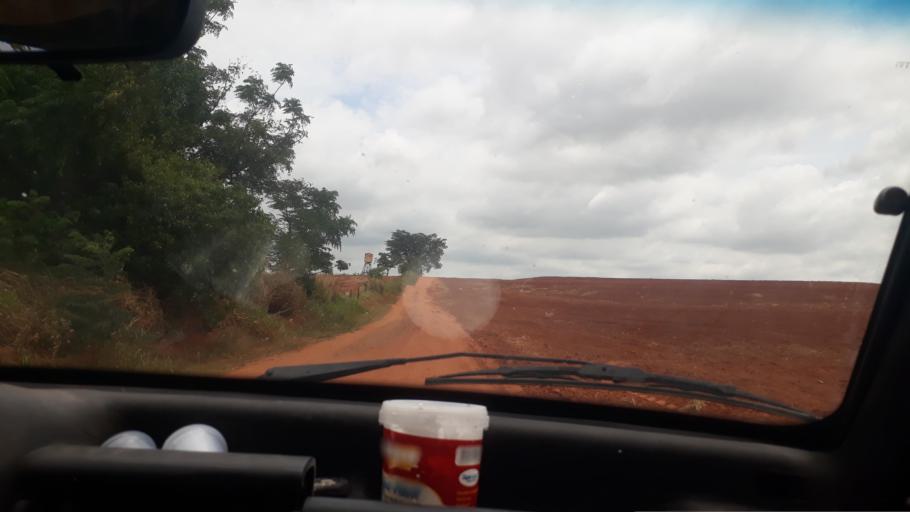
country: BR
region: Sao Paulo
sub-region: Regente Feijo
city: Regente Feijo
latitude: -22.2560
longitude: -51.3004
